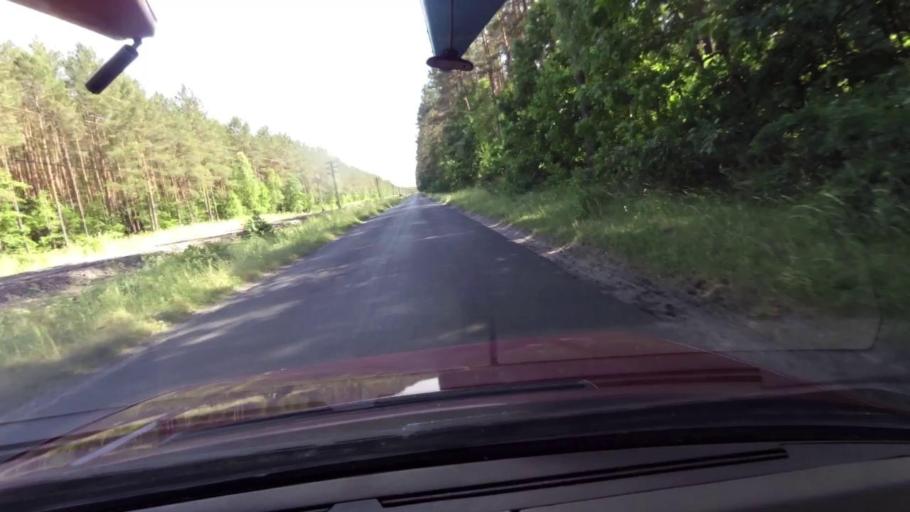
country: PL
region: Pomeranian Voivodeship
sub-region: Powiat slupski
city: Kepice
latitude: 54.2313
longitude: 16.8937
